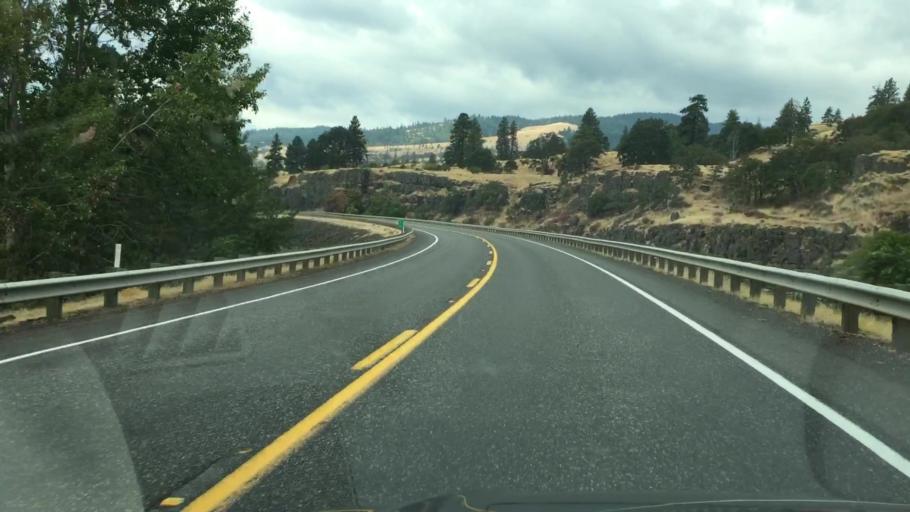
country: US
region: Oregon
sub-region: Wasco County
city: Chenoweth
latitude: 45.7105
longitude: -121.3426
